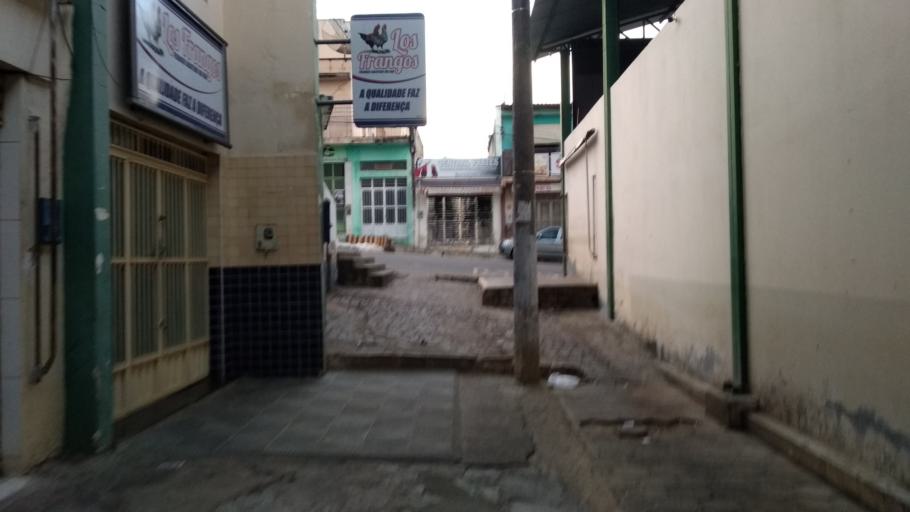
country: BR
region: Bahia
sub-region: Caetite
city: Caetite
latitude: -14.0659
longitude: -42.4905
